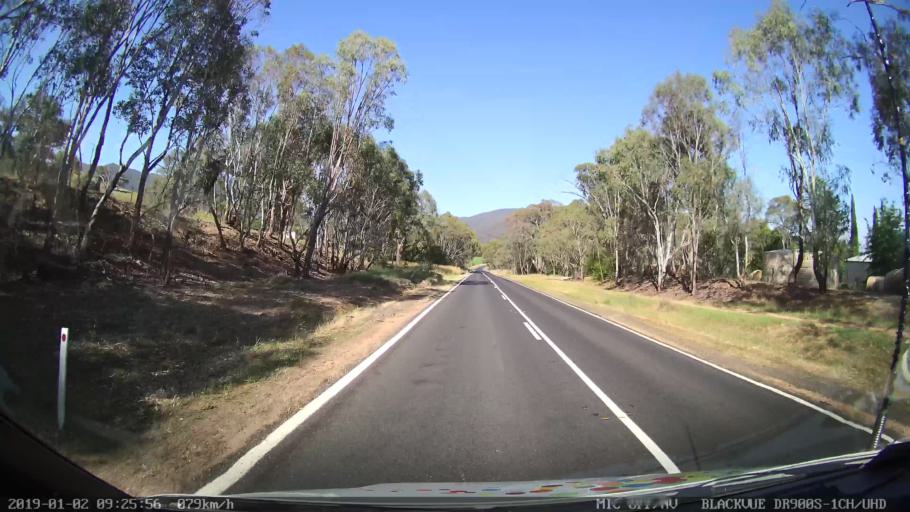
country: AU
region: New South Wales
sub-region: Tumut Shire
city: Tumut
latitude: -35.3644
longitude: 148.2796
